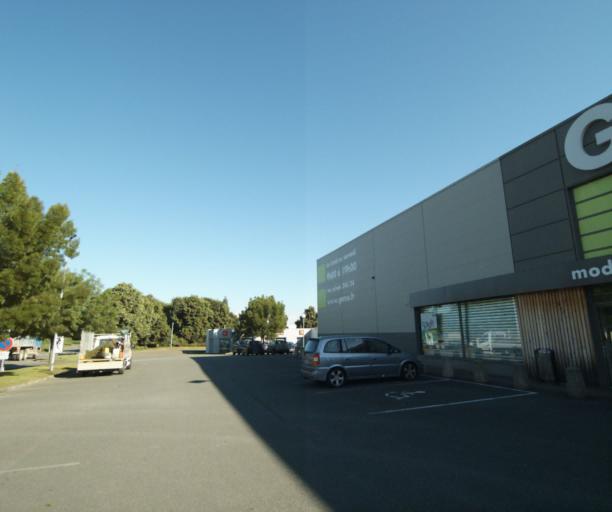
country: FR
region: Pays de la Loire
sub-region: Departement de la Mayenne
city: Laval
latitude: 48.0524
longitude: -0.7390
